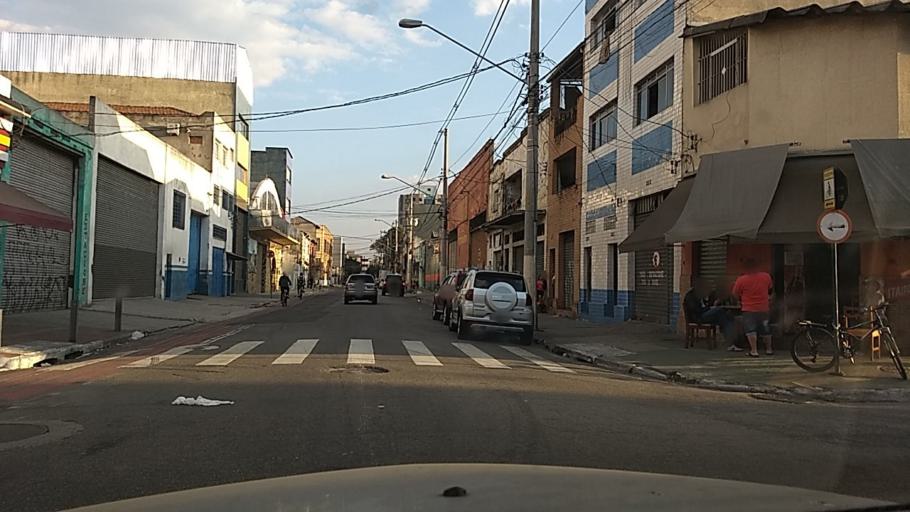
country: BR
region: Sao Paulo
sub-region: Sao Paulo
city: Sao Paulo
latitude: -23.5310
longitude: -46.6233
